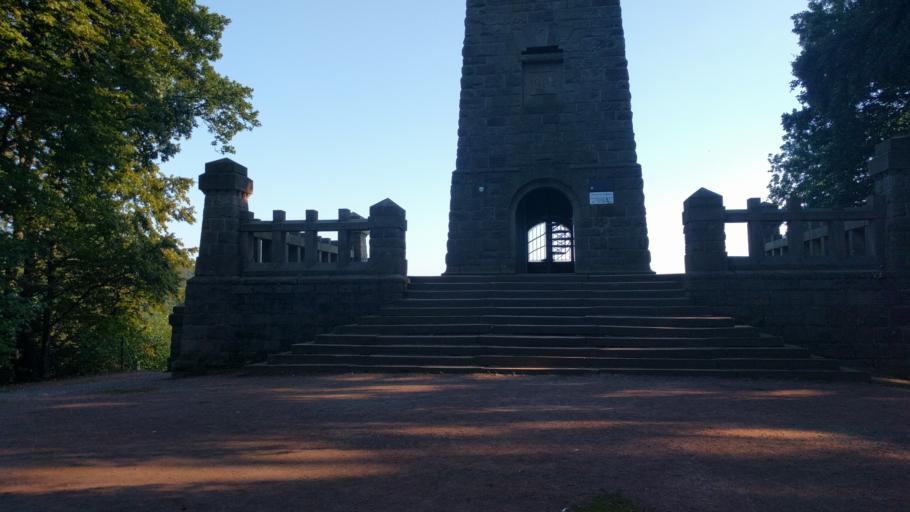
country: DE
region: North Rhine-Westphalia
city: Witten
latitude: 51.4260
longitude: 7.3518
